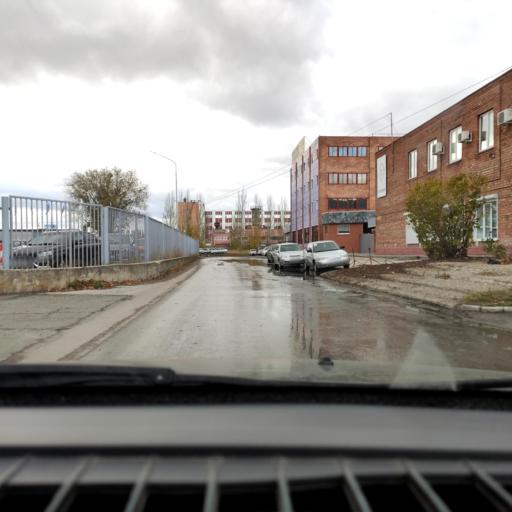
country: RU
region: Samara
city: Tol'yatti
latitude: 53.5587
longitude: 49.2964
